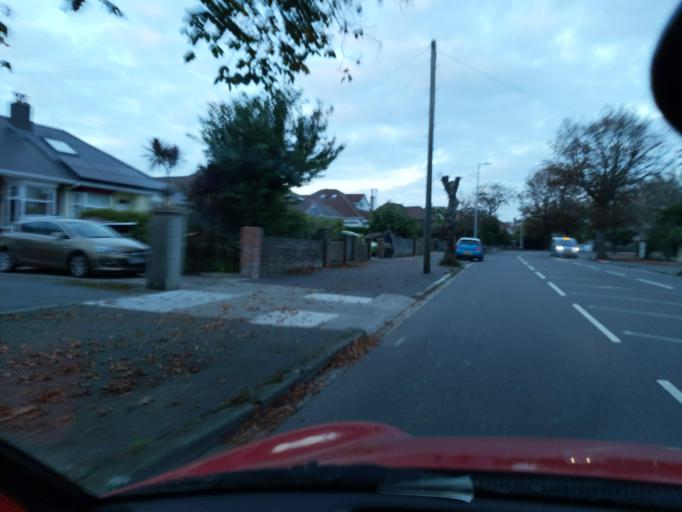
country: GB
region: England
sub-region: Plymouth
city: Plymouth
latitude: 50.3936
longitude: -4.1592
